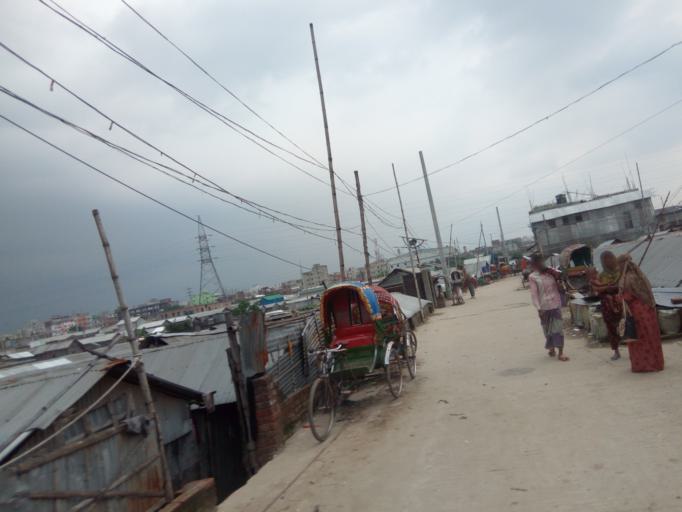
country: BD
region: Dhaka
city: Azimpur
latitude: 23.7363
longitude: 90.3595
